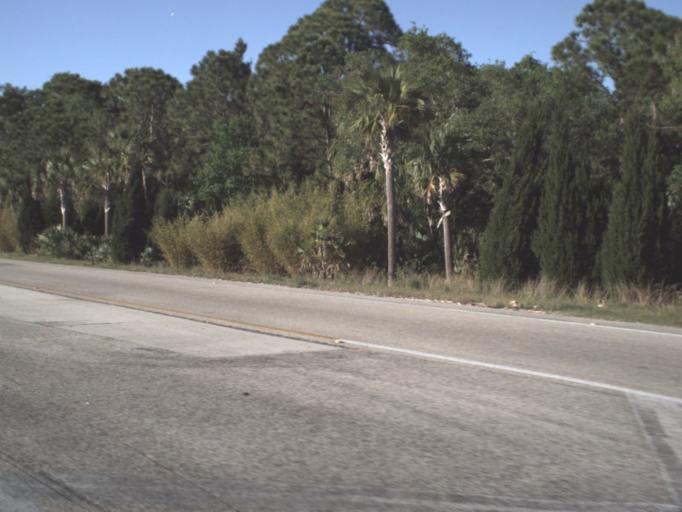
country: US
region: Florida
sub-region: Brevard County
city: South Patrick Shores
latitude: 28.2247
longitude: -80.7167
